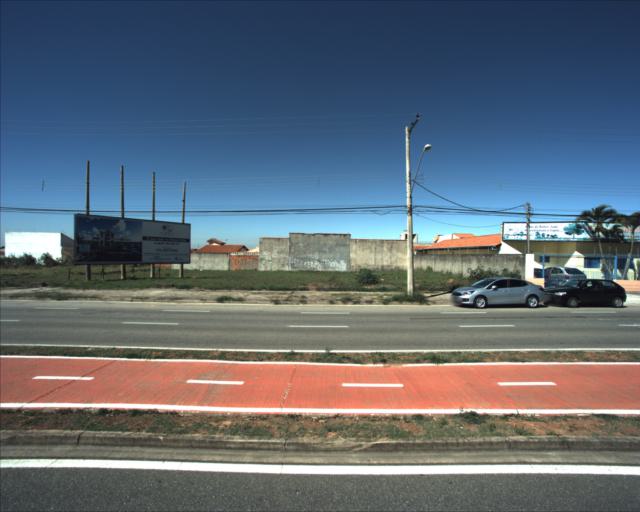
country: BR
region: Sao Paulo
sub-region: Sorocaba
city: Sorocaba
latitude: -23.4860
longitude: -47.5108
